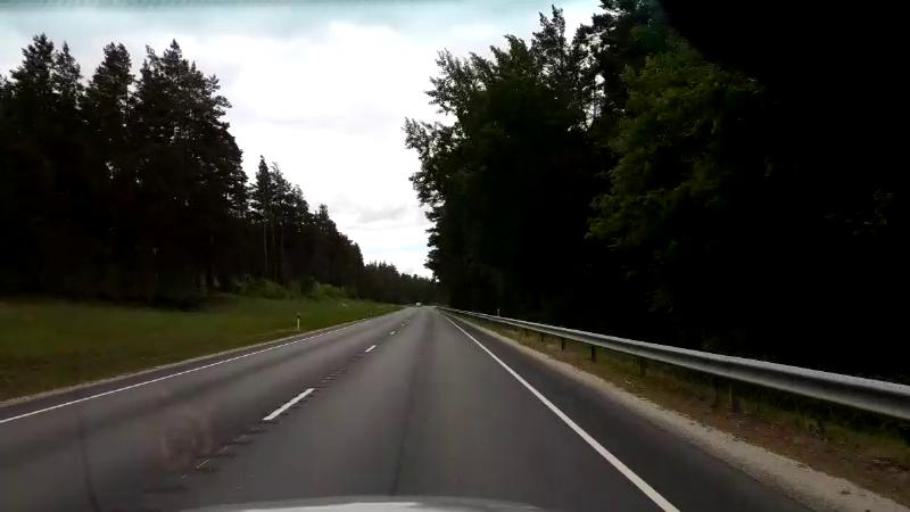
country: EE
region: Paernumaa
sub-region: Paernu linn
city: Parnu
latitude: 58.1633
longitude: 24.4975
